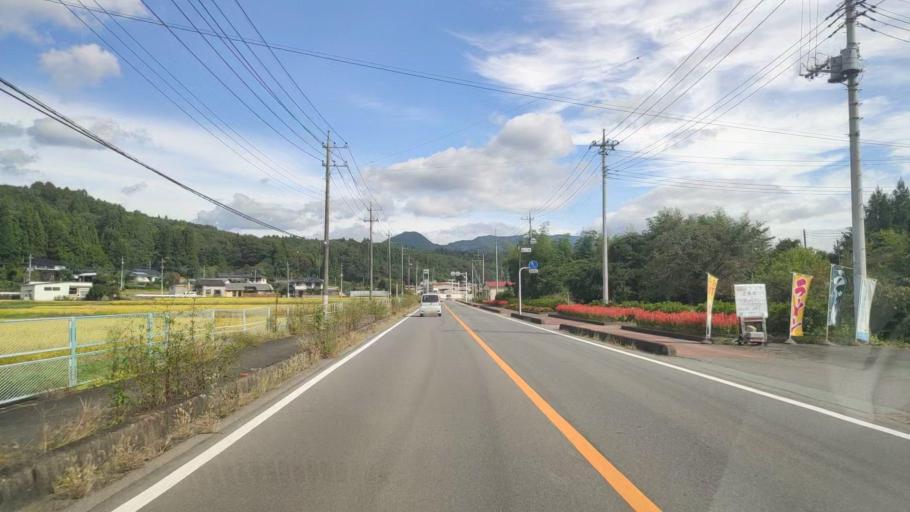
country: JP
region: Gunma
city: Nakanojomachi
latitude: 36.5974
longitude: 138.8632
